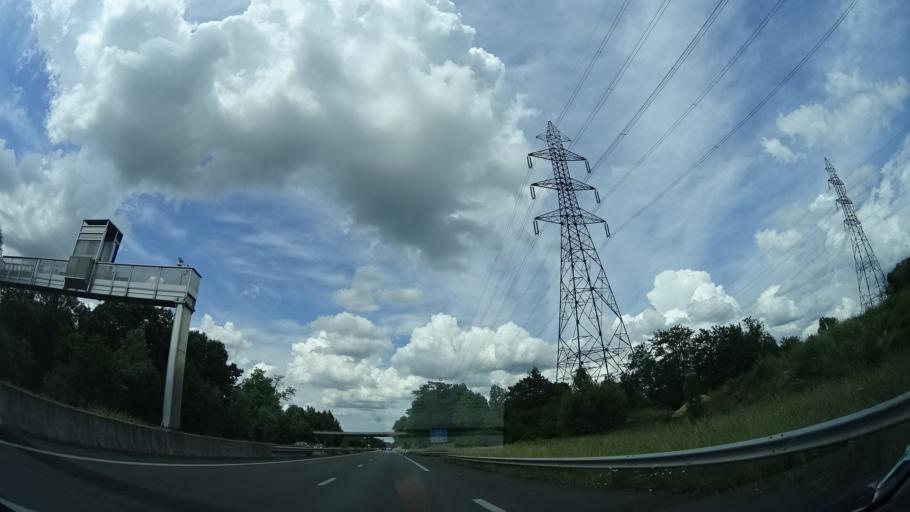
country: FR
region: Aquitaine
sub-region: Departement de la Gironde
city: Pugnac
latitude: 45.0955
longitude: -0.4749
